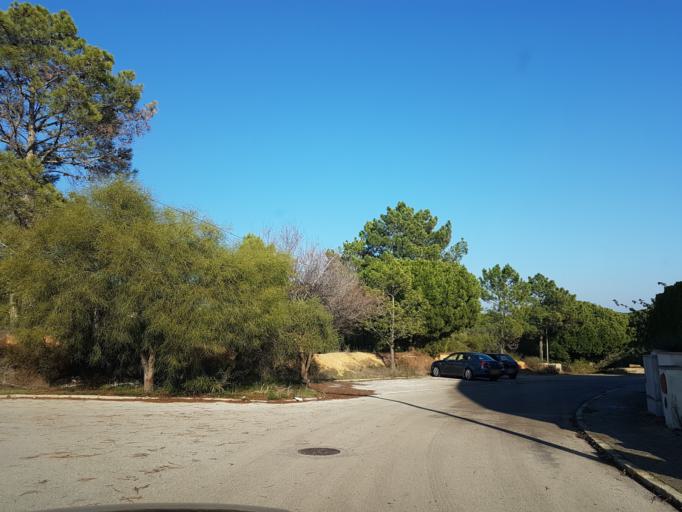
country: PT
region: Faro
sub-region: Albufeira
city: Ferreiras
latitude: 37.0961
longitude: -8.2028
